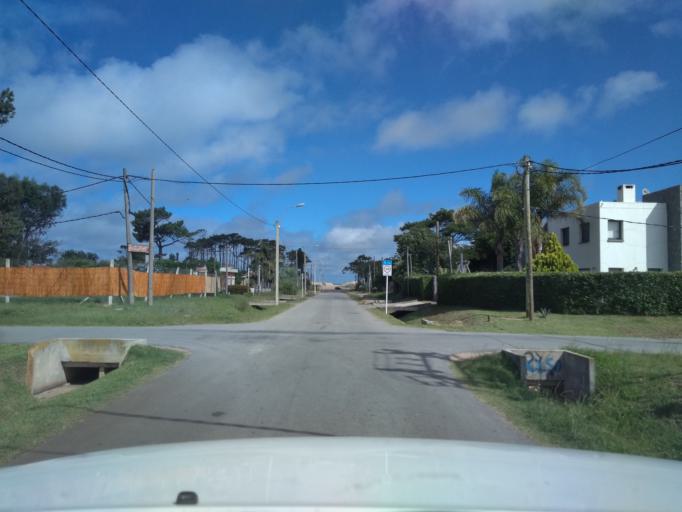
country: UY
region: Canelones
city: Barra de Carrasco
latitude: -34.8397
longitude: -55.9670
